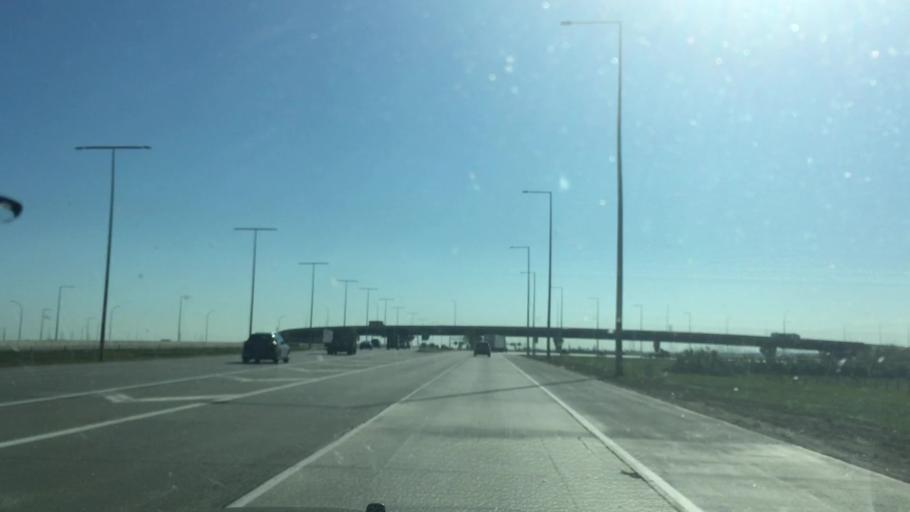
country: CA
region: Alberta
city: Edmonton
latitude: 53.4358
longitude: -113.5014
